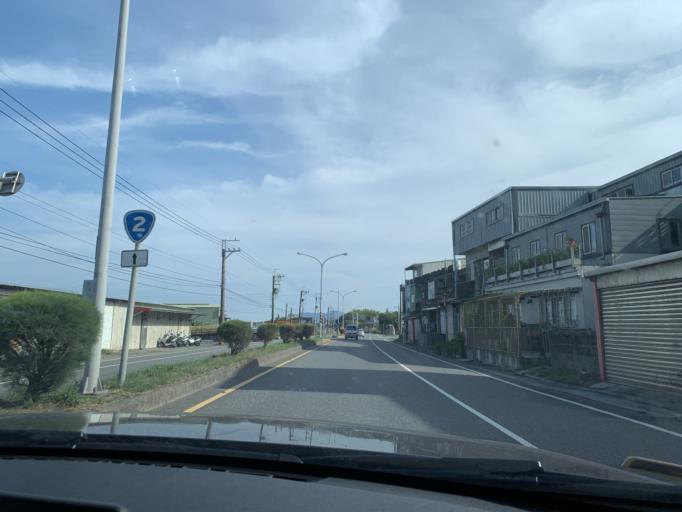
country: TW
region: Taiwan
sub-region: Yilan
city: Yilan
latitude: 24.7352
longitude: 121.8183
